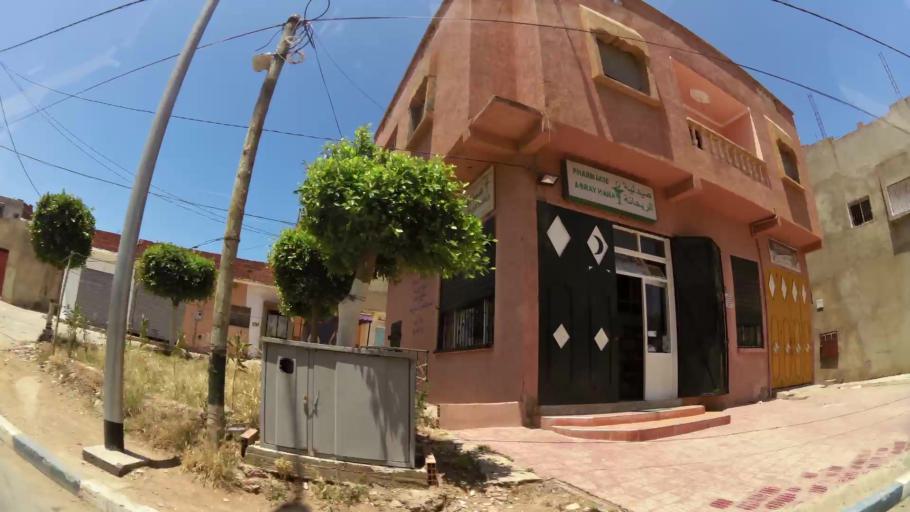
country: MA
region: Gharb-Chrarda-Beni Hssen
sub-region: Kenitra Province
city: Kenitra
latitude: 34.2608
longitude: -6.6458
